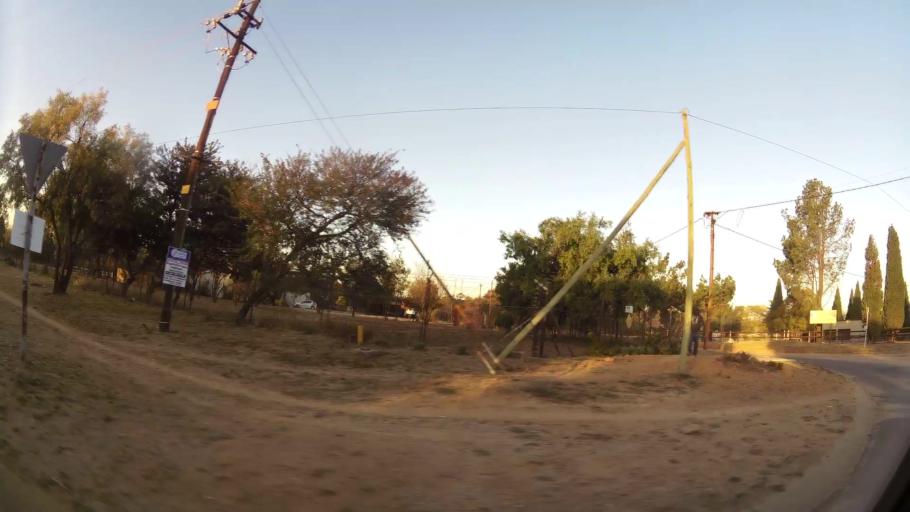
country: ZA
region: Gauteng
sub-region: City of Johannesburg Metropolitan Municipality
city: Diepsloot
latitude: -25.9702
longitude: 28.0467
